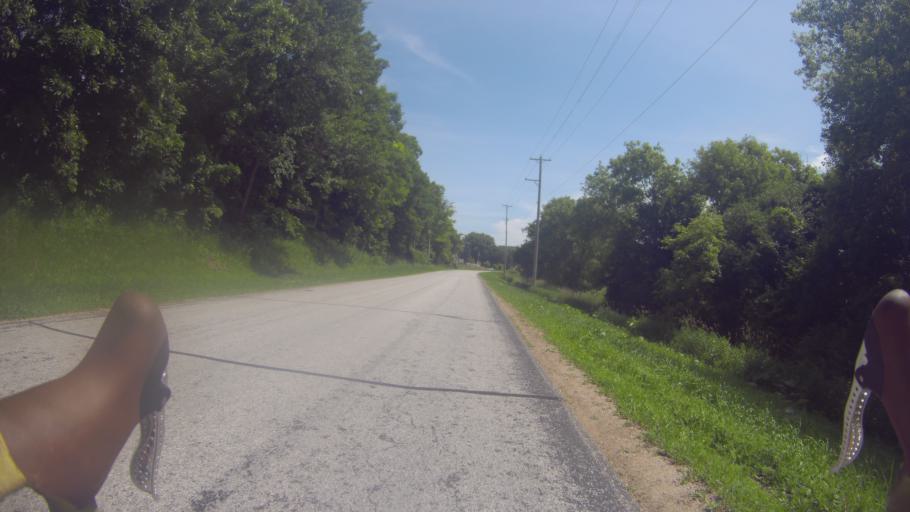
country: US
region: Wisconsin
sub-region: Dane County
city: Deerfield
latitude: 43.0428
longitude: -89.0504
